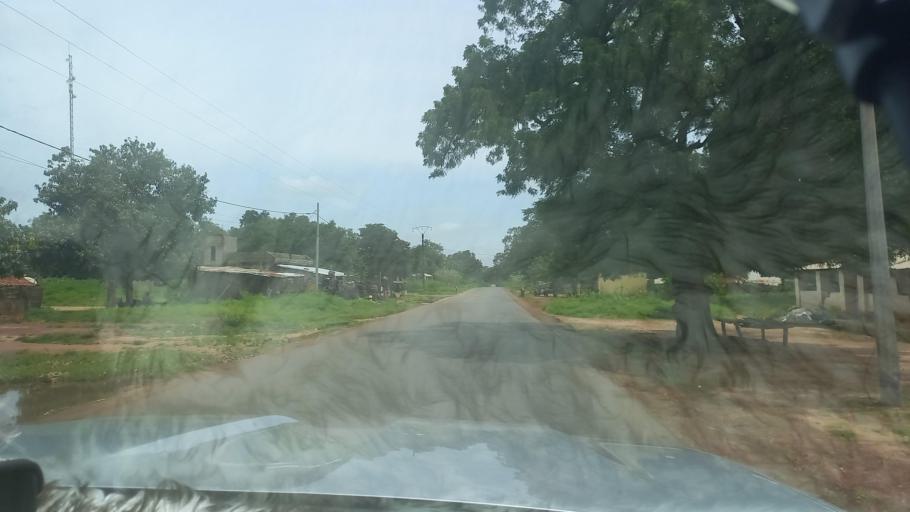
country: SN
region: Kolda
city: Marsassoum
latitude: 12.9645
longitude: -15.9728
